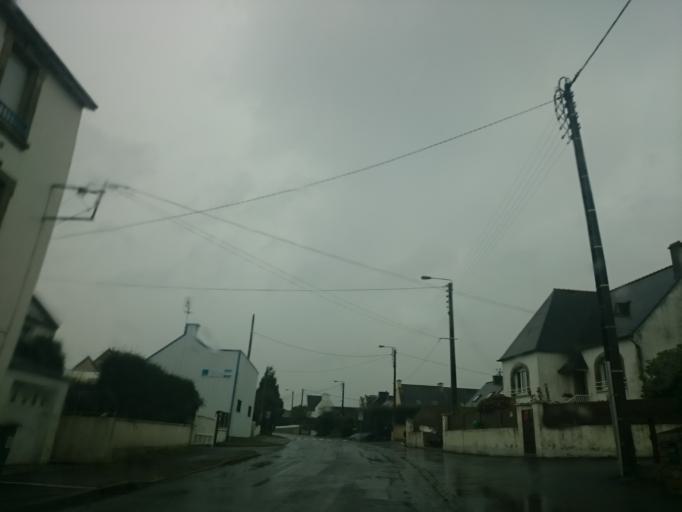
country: FR
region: Brittany
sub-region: Departement du Finistere
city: Plouvien
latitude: 48.5303
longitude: -4.4573
